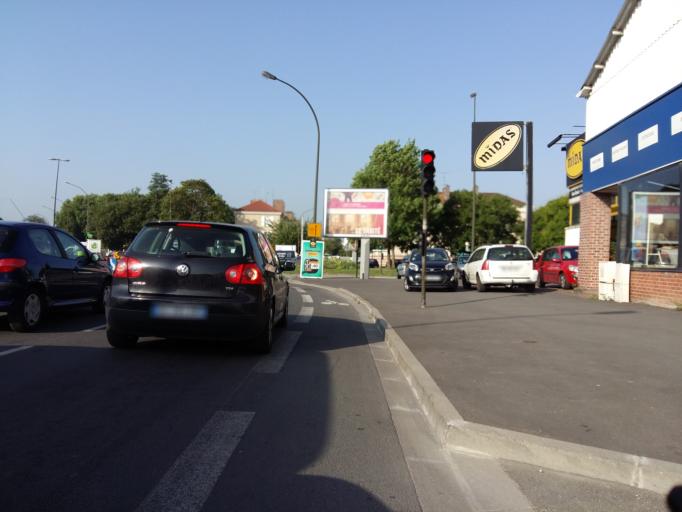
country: FR
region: Picardie
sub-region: Departement de la Somme
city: Amiens
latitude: 49.9023
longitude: 2.2844
